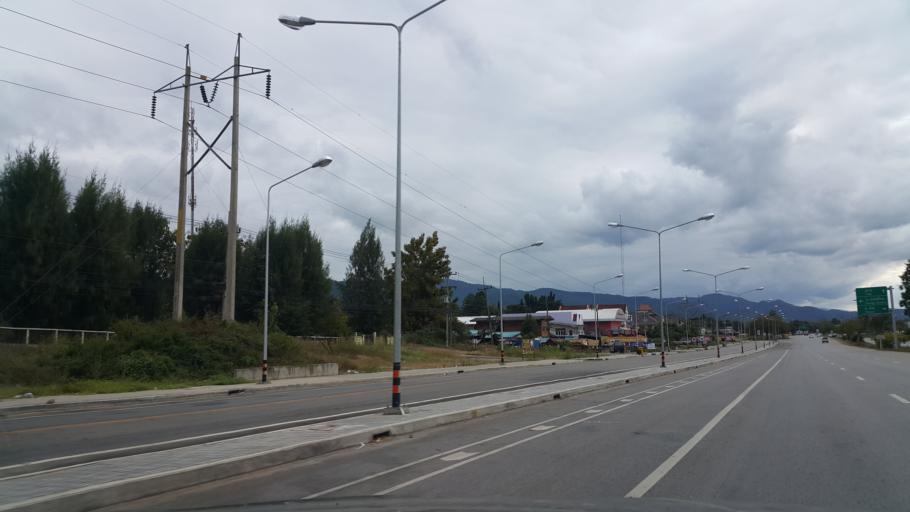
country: TH
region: Lampang
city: Thoen
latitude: 17.6337
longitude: 99.2391
